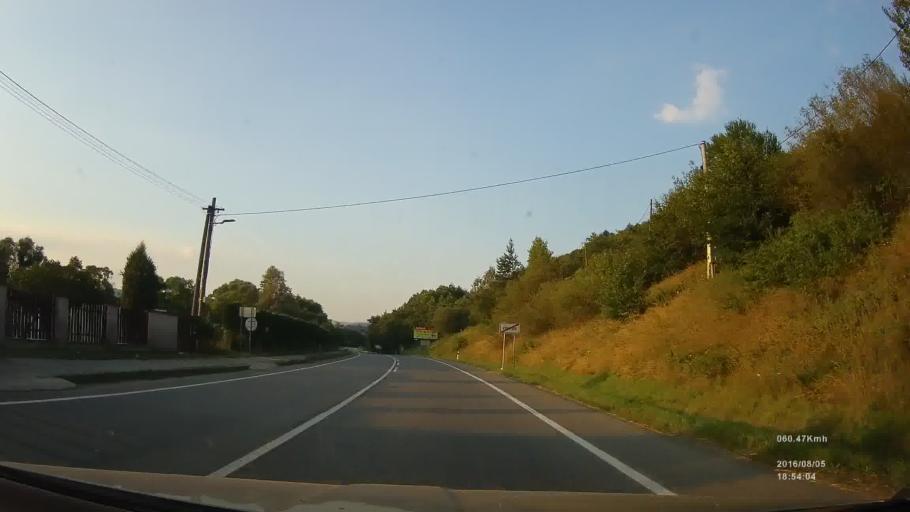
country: SK
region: Presovsky
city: Stropkov
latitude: 49.2215
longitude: 21.6629
